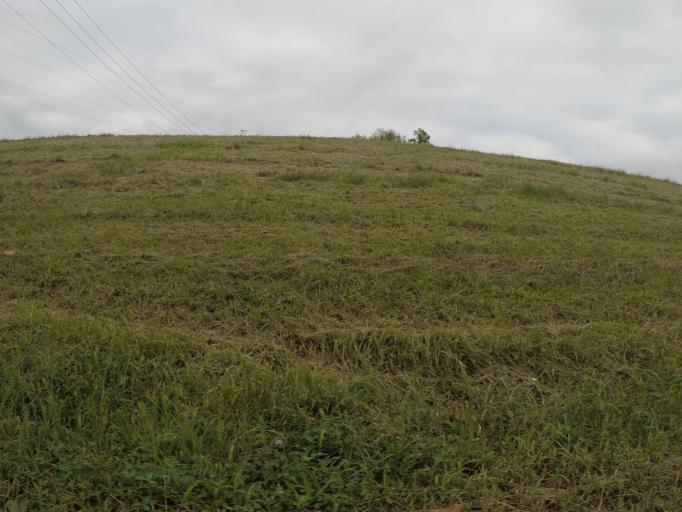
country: US
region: West Virginia
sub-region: Cabell County
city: Huntington
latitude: 38.4188
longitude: -82.3894
